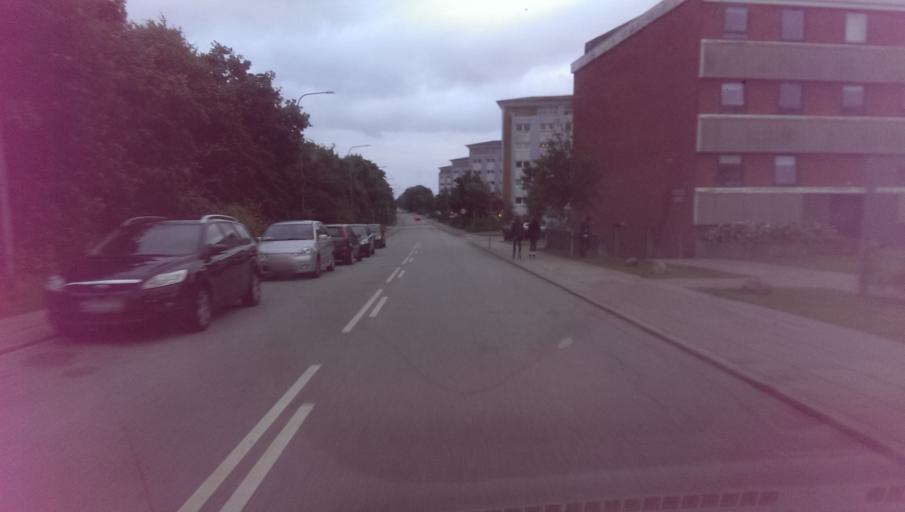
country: DK
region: South Denmark
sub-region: Esbjerg Kommune
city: Esbjerg
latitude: 55.4714
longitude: 8.4874
